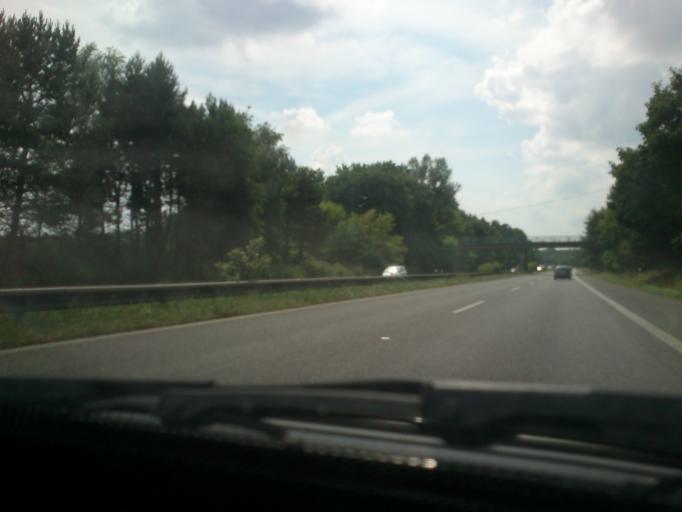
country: CZ
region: Central Bohemia
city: Benatky nad Jizerou
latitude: 50.2747
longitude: 14.8191
